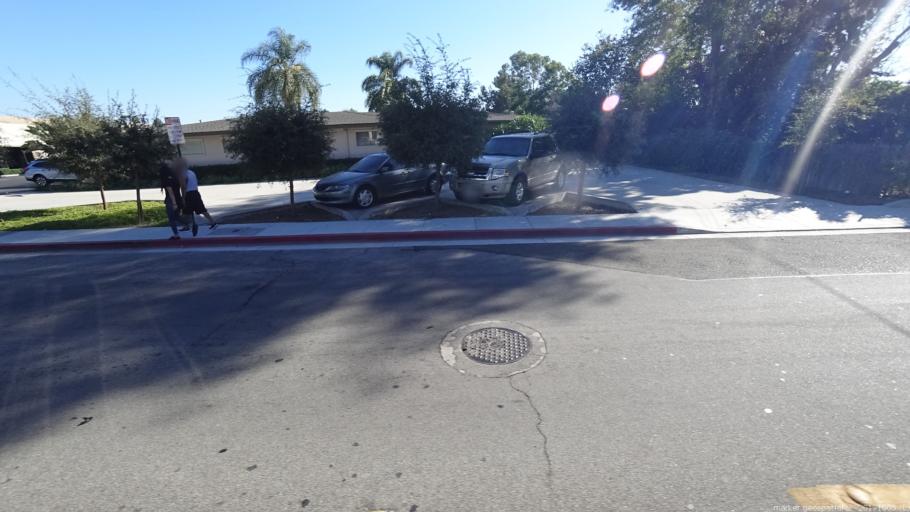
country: US
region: California
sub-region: Orange County
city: Garden Grove
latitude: 33.7777
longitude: -117.9526
